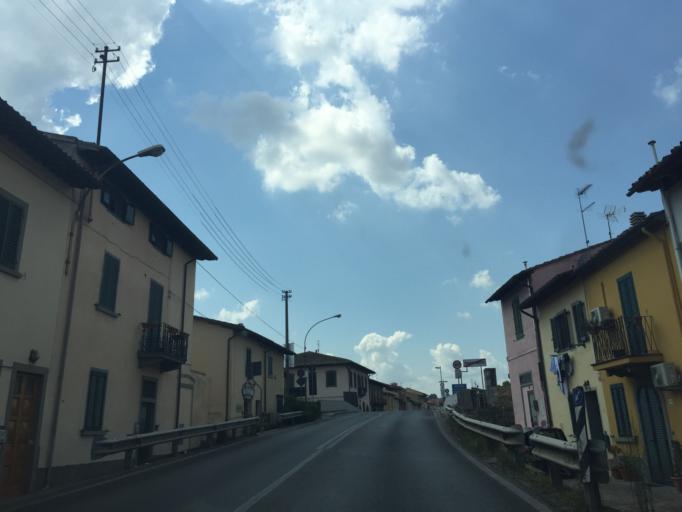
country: IT
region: Tuscany
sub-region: Provincia di Prato
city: Poggio A Caiano
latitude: 43.8142
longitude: 11.0625
